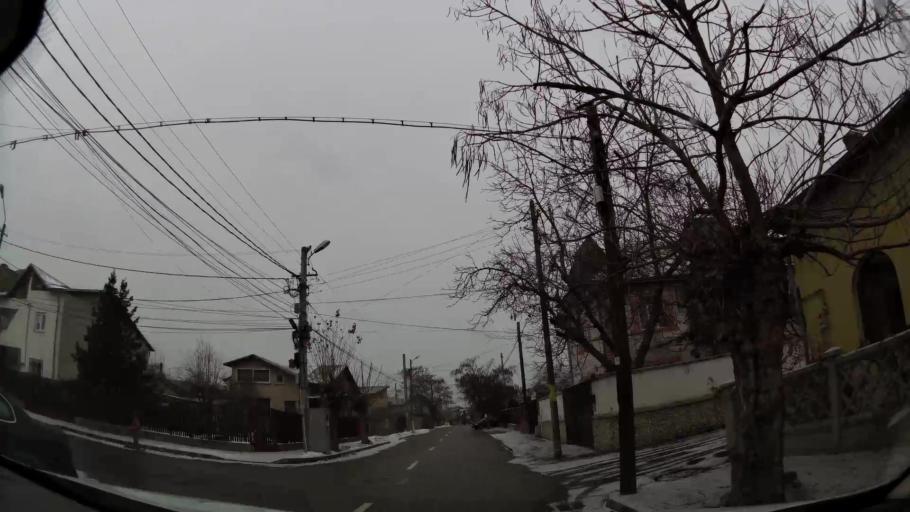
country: RO
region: Dambovita
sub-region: Municipiul Targoviste
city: Targoviste
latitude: 44.9370
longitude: 25.4519
